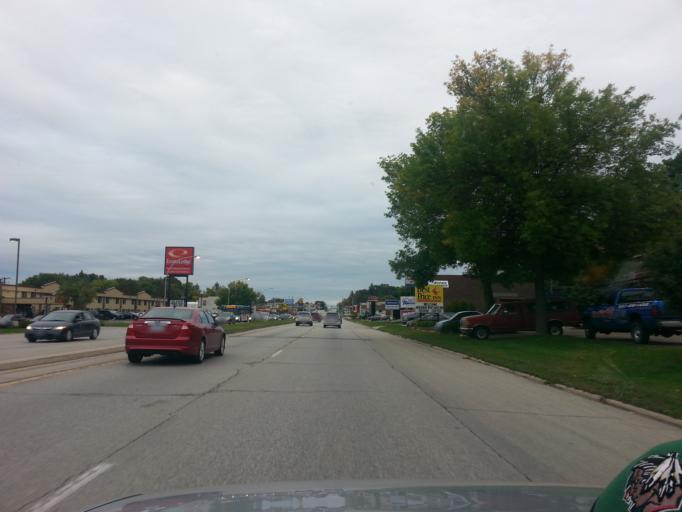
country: US
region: Minnesota
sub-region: Olmsted County
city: Rochester
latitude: 43.9959
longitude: -92.4633
